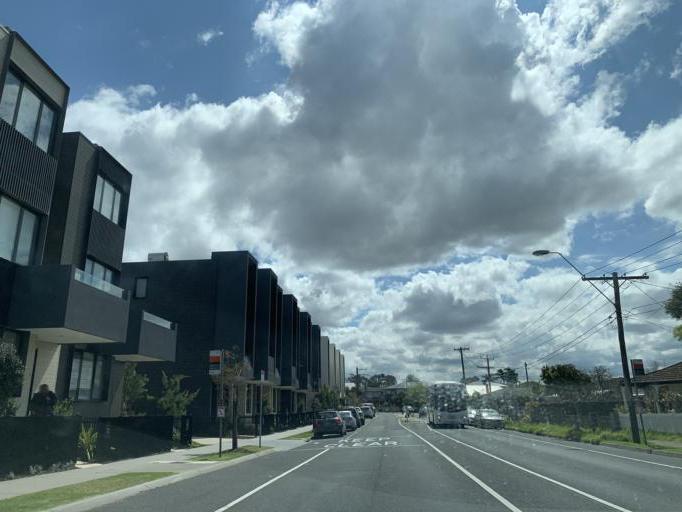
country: AU
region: Victoria
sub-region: Kingston
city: Mordialloc
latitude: -38.0089
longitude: 145.0899
